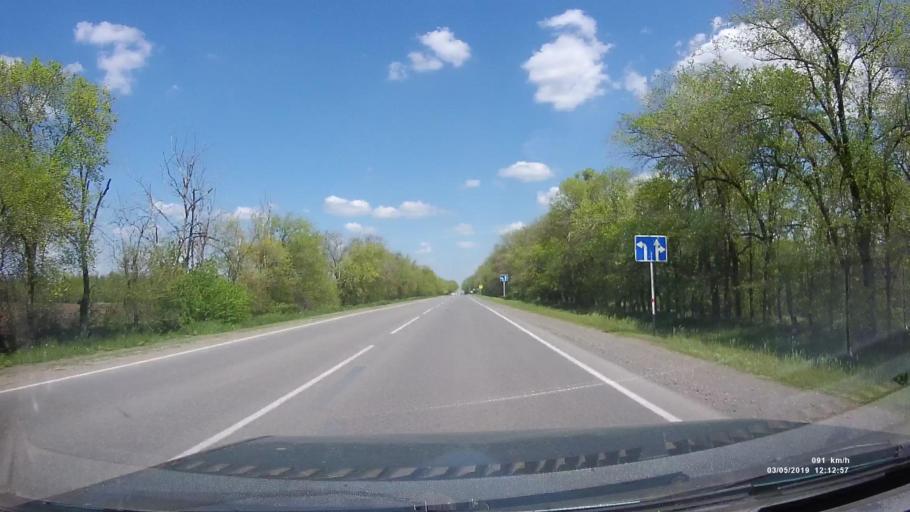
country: RU
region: Rostov
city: Bagayevskaya
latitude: 47.3274
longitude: 40.5510
